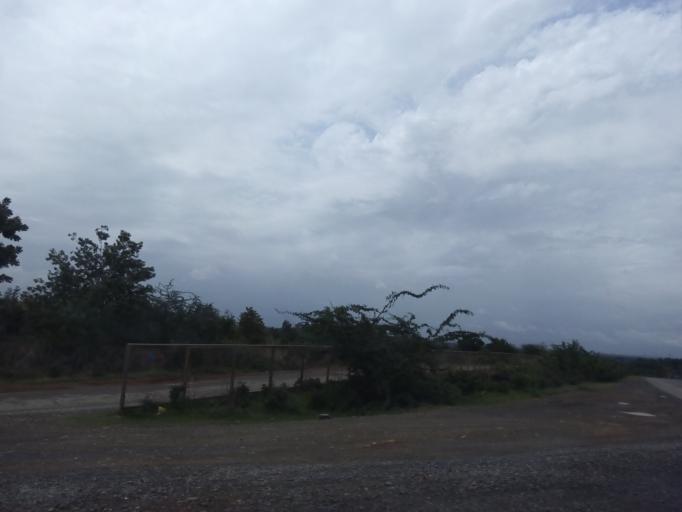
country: IN
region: Karnataka
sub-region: Haveri
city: Byadgi
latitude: 14.7023
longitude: 75.5215
